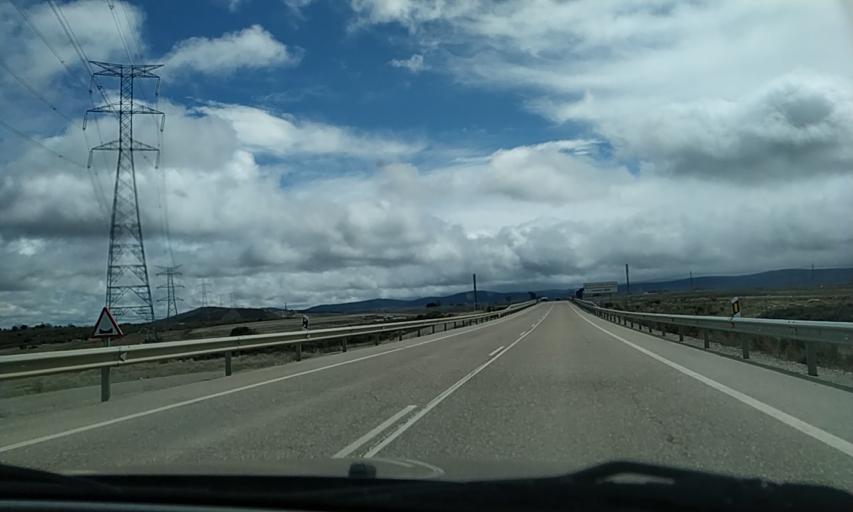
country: ES
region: Castille and Leon
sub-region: Provincia de Zamora
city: Villardeciervos
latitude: 41.9952
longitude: -6.2463
